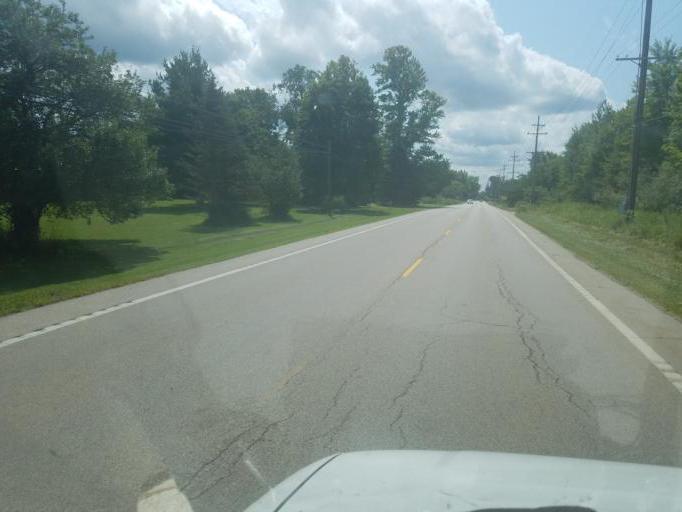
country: US
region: Ohio
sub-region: Ashtabula County
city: Roaming Shores
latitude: 41.6695
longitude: -80.8577
